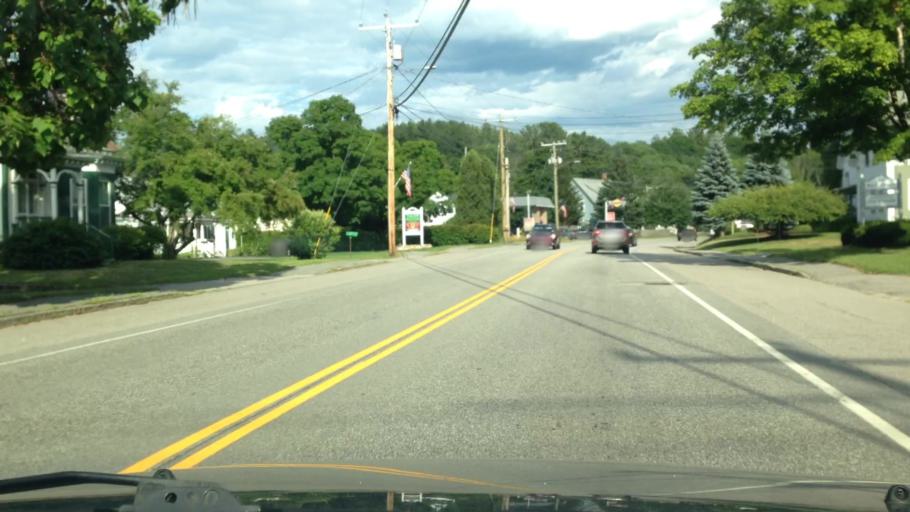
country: US
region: New Hampshire
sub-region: Cheshire County
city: Marlborough
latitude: 42.9075
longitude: -72.2130
